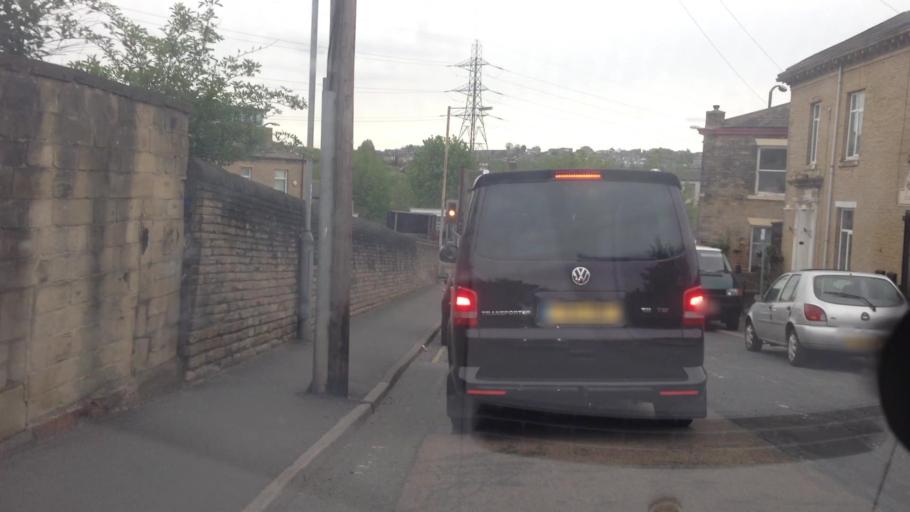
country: GB
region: England
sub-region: Calderdale
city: Brighouse
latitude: 53.6984
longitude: -1.7798
